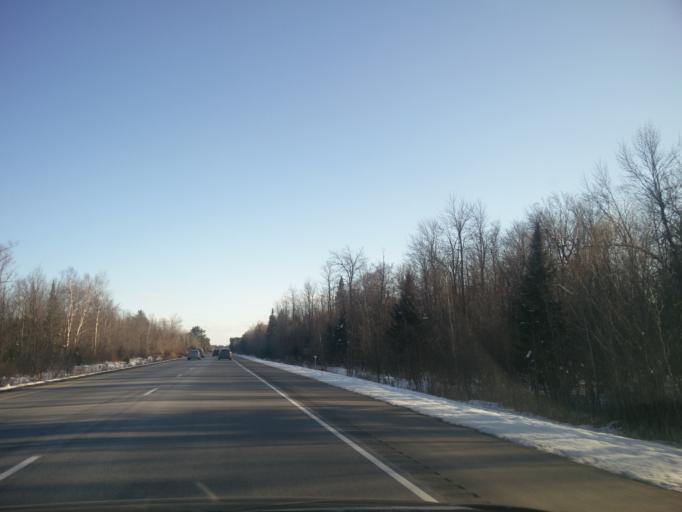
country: CA
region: Ontario
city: Prescott
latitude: 44.8119
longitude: -75.5162
